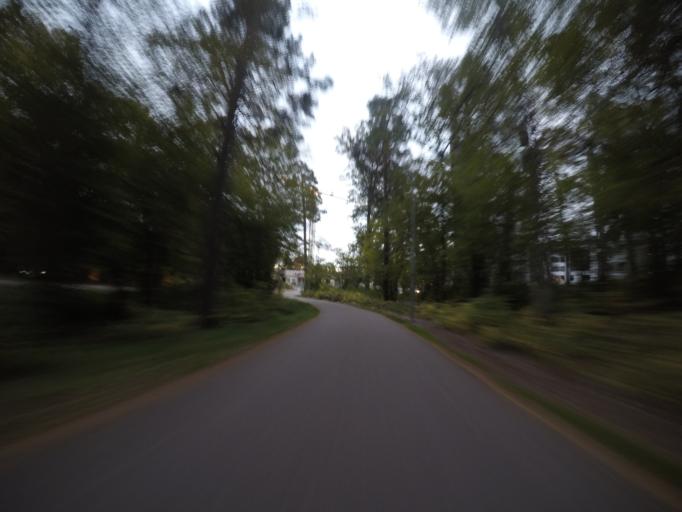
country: SE
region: Vaestmanland
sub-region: Vasteras
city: Vasteras
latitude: 59.6045
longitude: 16.5794
